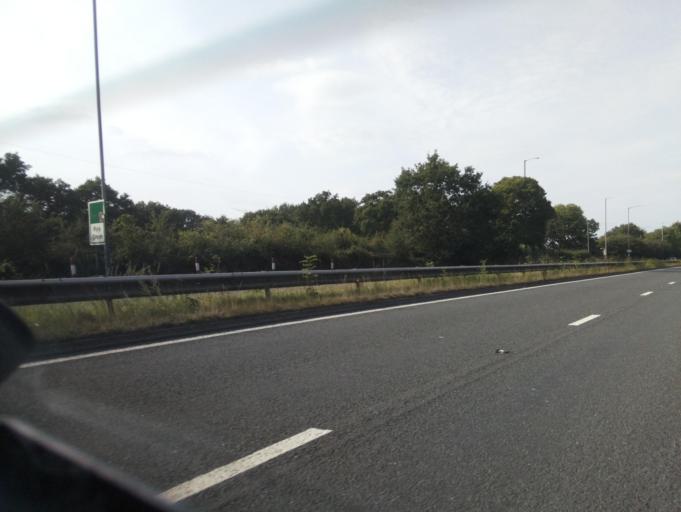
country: GB
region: England
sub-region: Solihull
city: Tidbury Green
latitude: 52.3261
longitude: -1.8675
